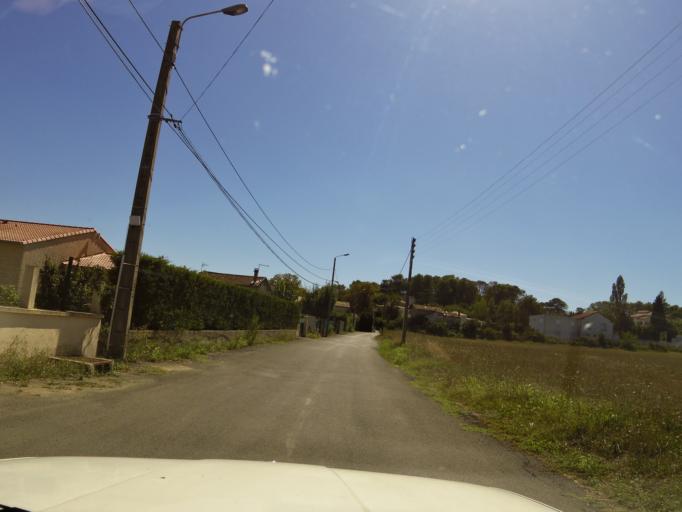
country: FR
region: Languedoc-Roussillon
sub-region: Departement du Gard
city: Ales
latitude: 44.1125
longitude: 4.1106
